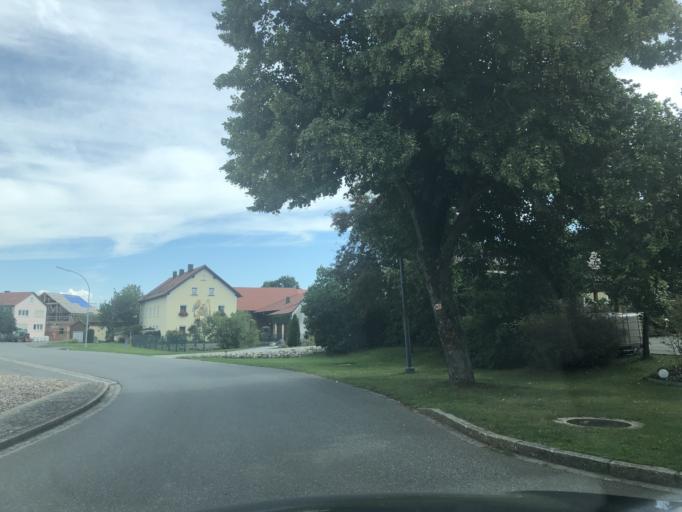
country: DE
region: Bavaria
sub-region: Upper Palatinate
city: Grafenwohr
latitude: 49.7356
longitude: 11.8823
